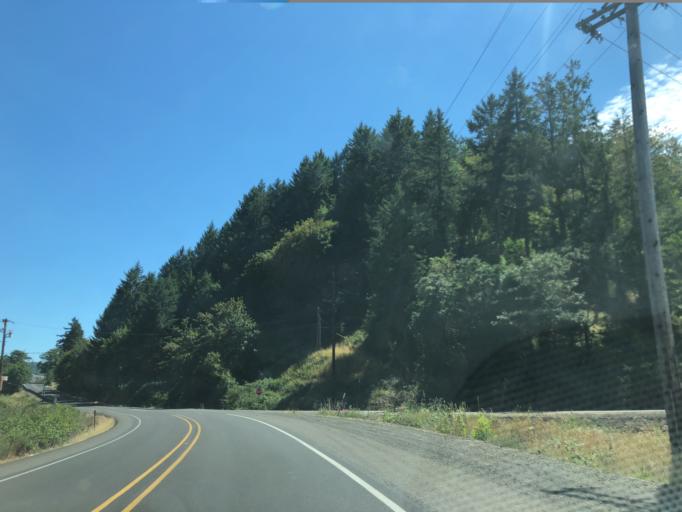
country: US
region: Oregon
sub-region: Douglas County
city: Yoncalla
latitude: 43.5809
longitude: -123.2809
